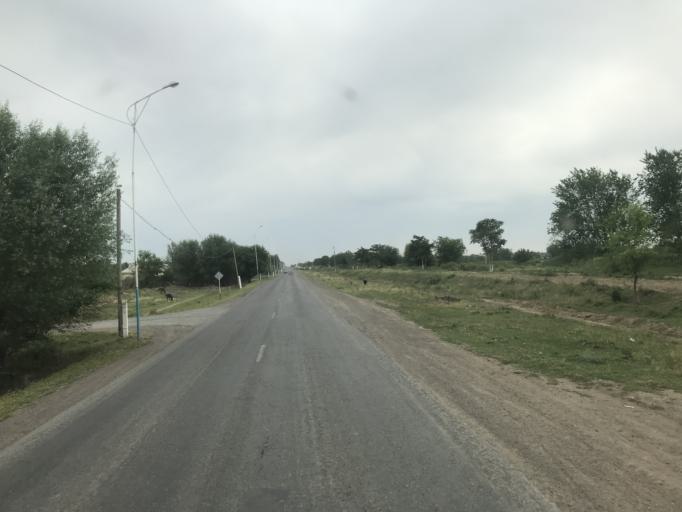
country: KZ
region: Ongtustik Qazaqstan
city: Asykata
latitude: 40.9413
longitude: 68.4146
